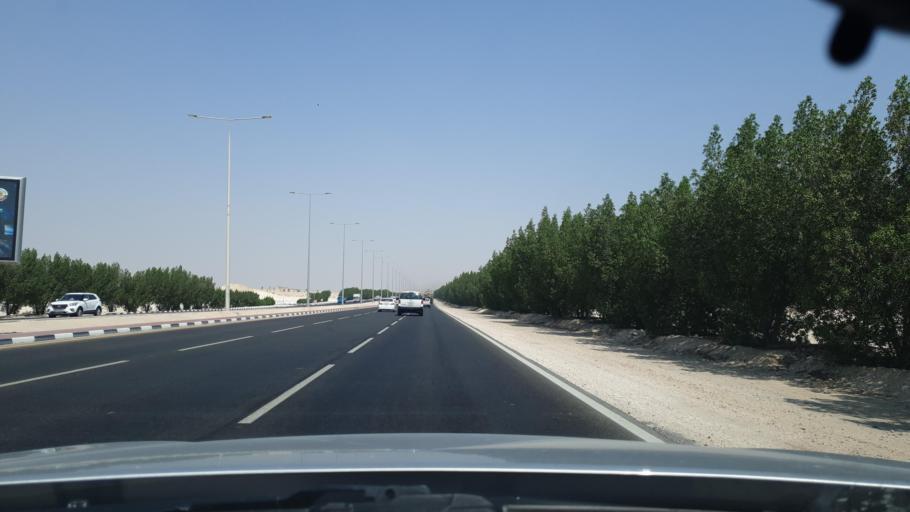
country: QA
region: Al Khawr
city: Al Khawr
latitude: 25.6967
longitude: 51.5022
